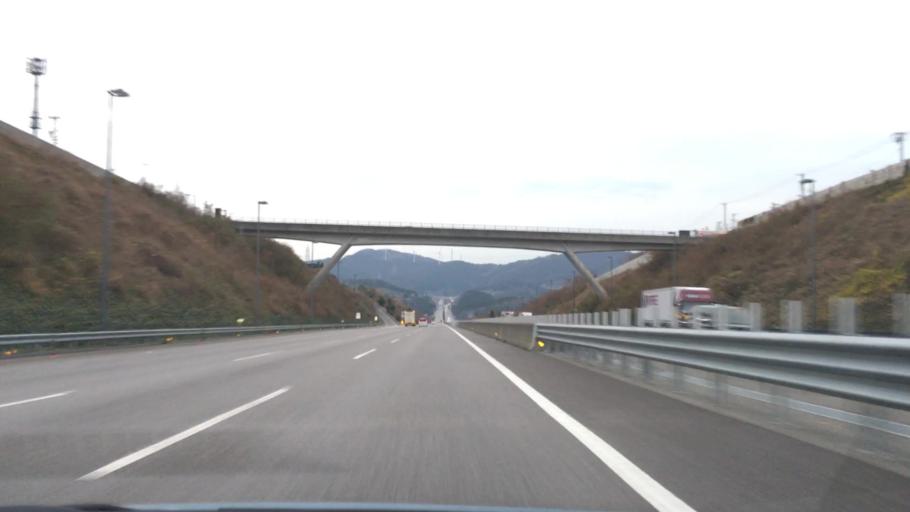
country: JP
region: Shizuoka
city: Hamakita
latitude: 34.8395
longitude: 137.7592
